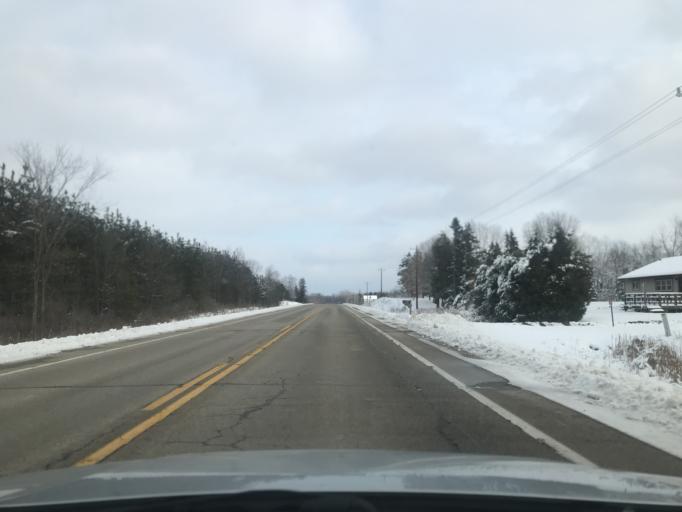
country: US
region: Wisconsin
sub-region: Oconto County
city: Oconto Falls
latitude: 44.8872
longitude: -88.0246
